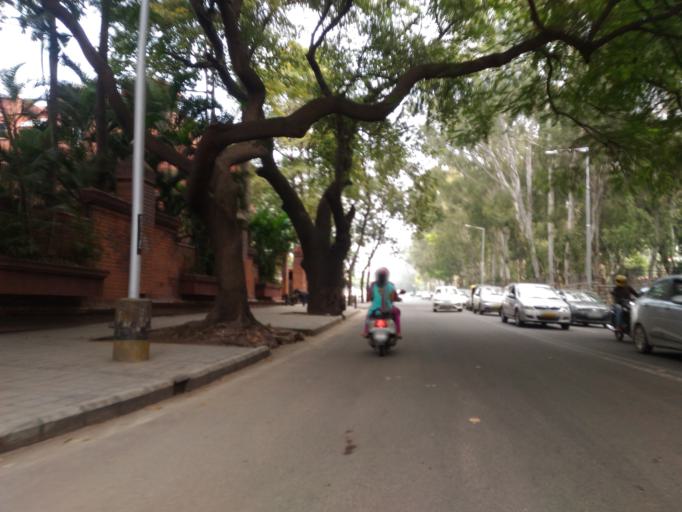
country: IN
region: Karnataka
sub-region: Bangalore Urban
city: Bangalore
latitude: 12.9582
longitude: 77.6061
